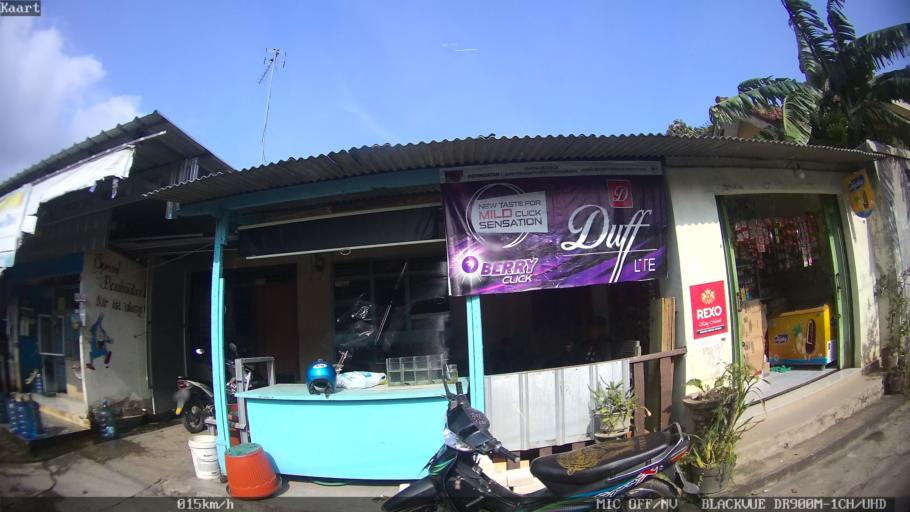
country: ID
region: Lampung
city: Kedaton
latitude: -5.3900
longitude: 105.2653
